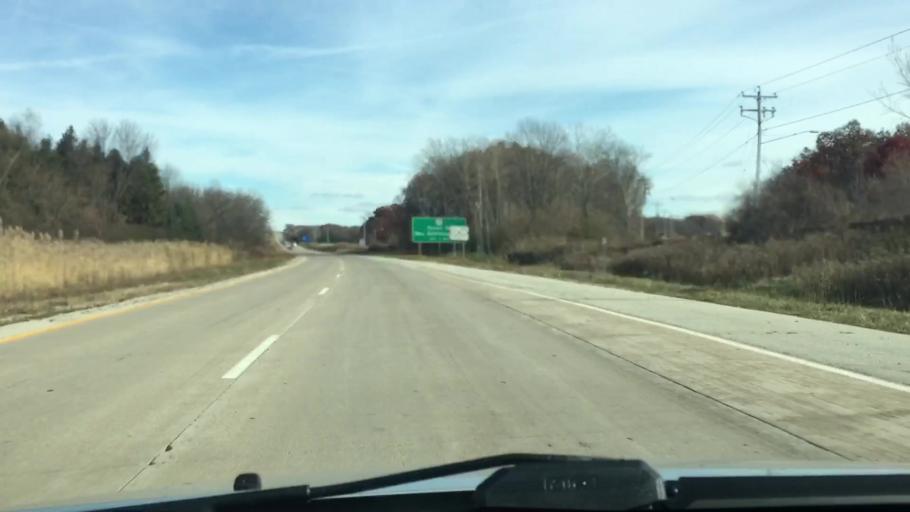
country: US
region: Wisconsin
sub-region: Brown County
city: Bellevue
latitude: 44.5246
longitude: -87.9300
